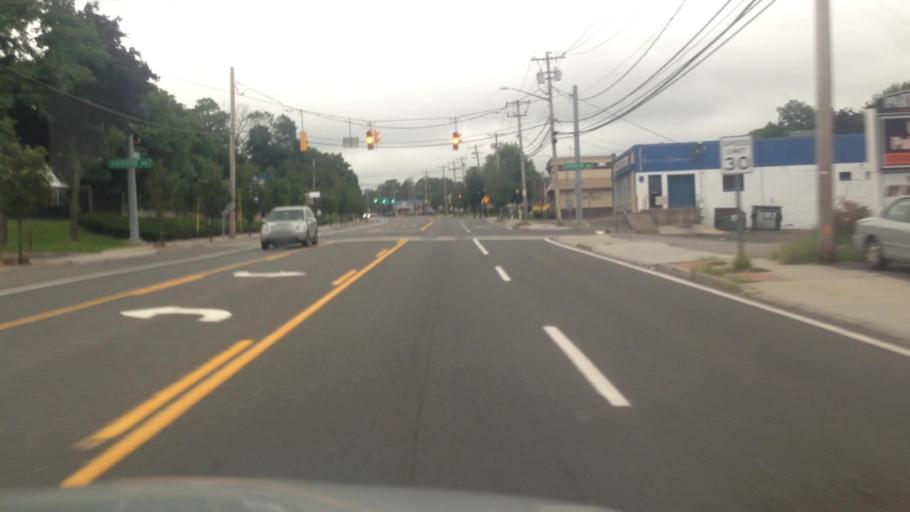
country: US
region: New York
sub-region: Suffolk County
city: Ronkonkoma
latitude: 40.8267
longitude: -73.1059
